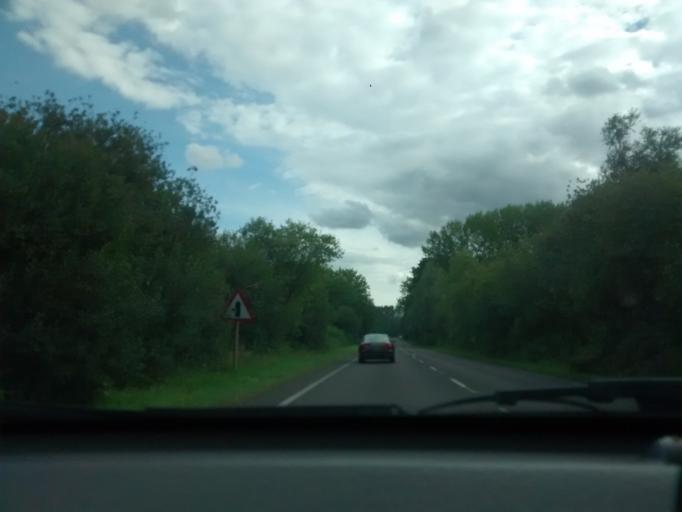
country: GB
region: England
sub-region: Norfolk
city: Downham Market
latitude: 52.5740
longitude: 0.3897
